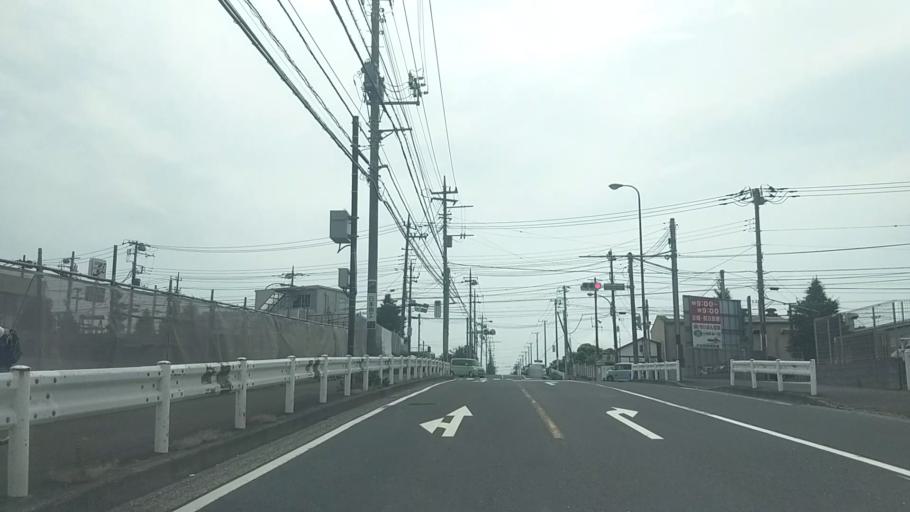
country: JP
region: Kanagawa
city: Fujisawa
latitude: 35.3898
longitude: 139.4582
